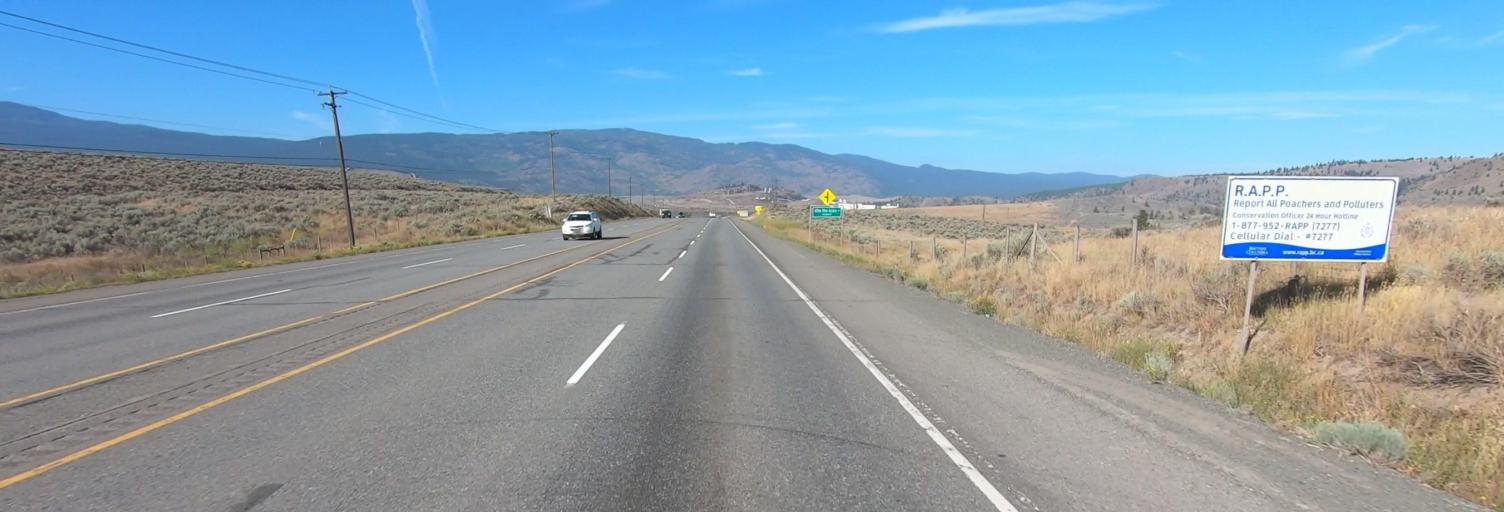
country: CA
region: British Columbia
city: Kamloops
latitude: 50.6690
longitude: -120.4855
